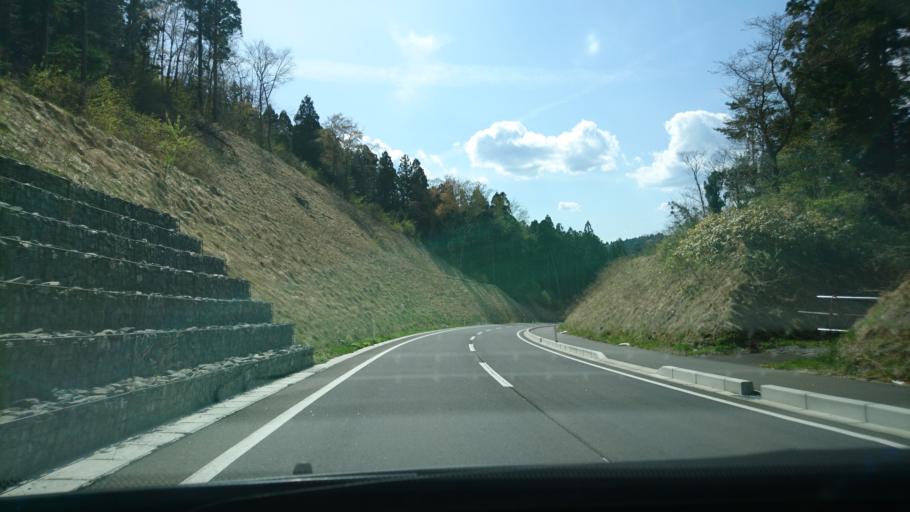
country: JP
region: Iwate
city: Ichinoseki
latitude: 38.9294
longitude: 141.4310
